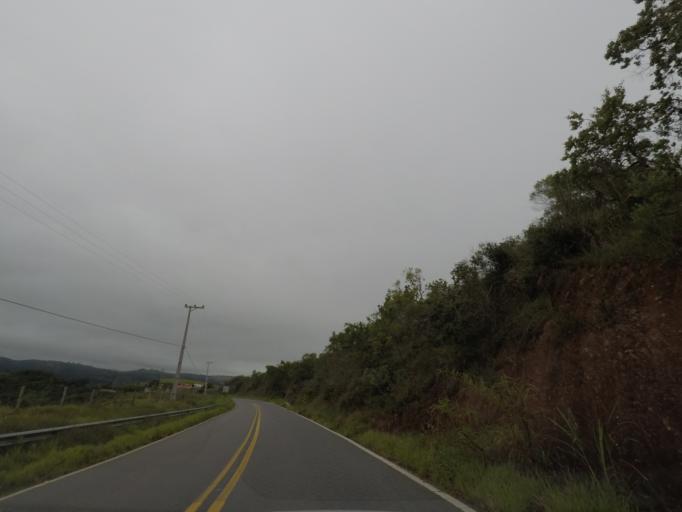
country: BR
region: Sao Paulo
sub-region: Cunha
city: Cunha
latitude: -23.0915
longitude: -44.9605
